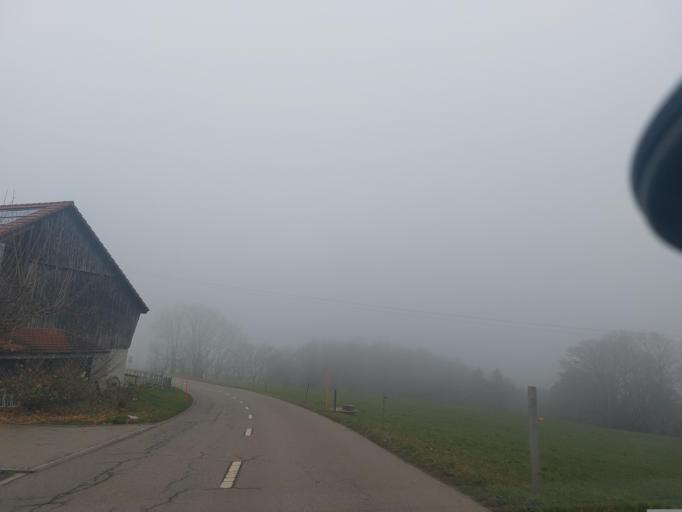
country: CH
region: Fribourg
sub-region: Veveyse District
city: Chatel-Saint-Denis
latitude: 46.5715
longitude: 6.8898
